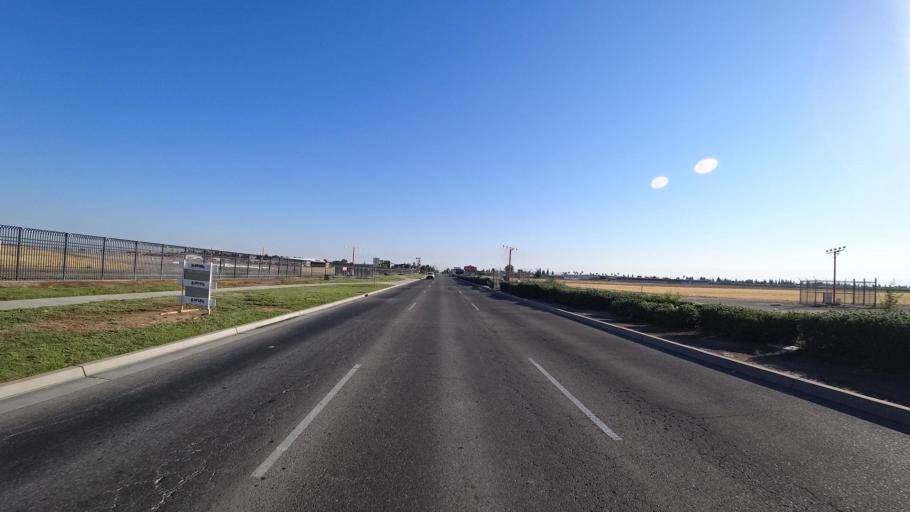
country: US
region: California
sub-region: Fresno County
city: Sunnyside
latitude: 36.7667
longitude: -119.7004
